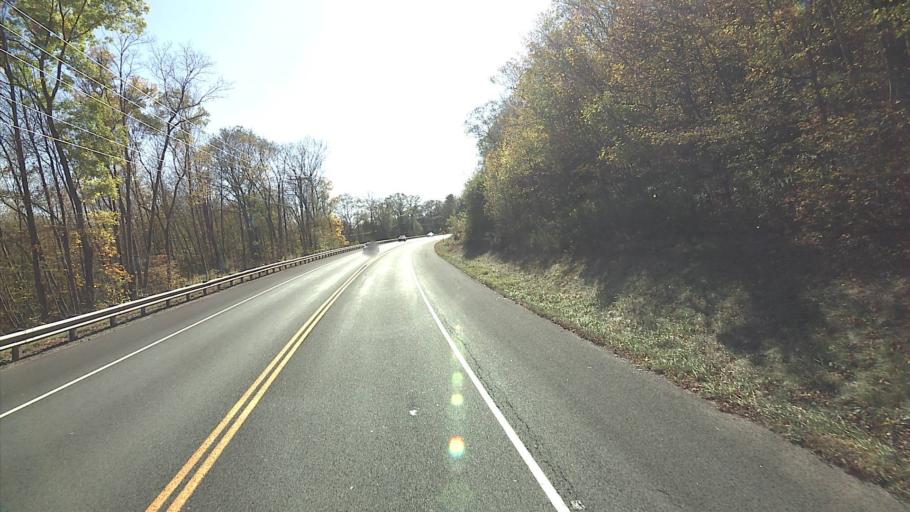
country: US
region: Connecticut
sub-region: Tolland County
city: Coventry Lake
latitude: 41.7699
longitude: -72.4079
